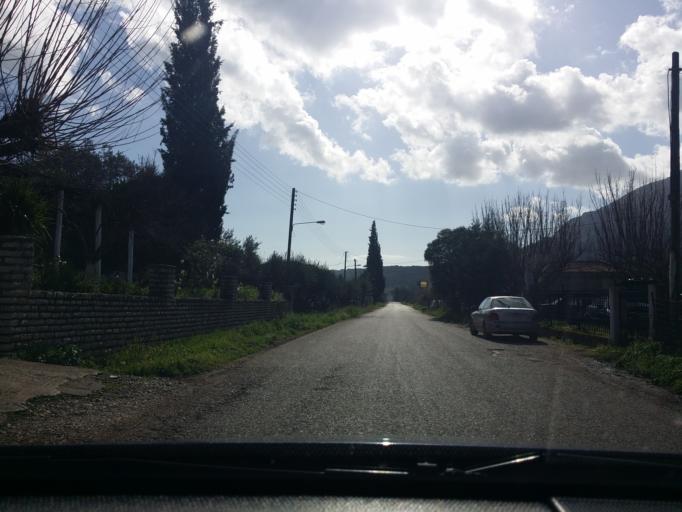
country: GR
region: West Greece
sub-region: Nomos Aitolias kai Akarnanias
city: Astakos
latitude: 38.5864
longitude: 21.0898
